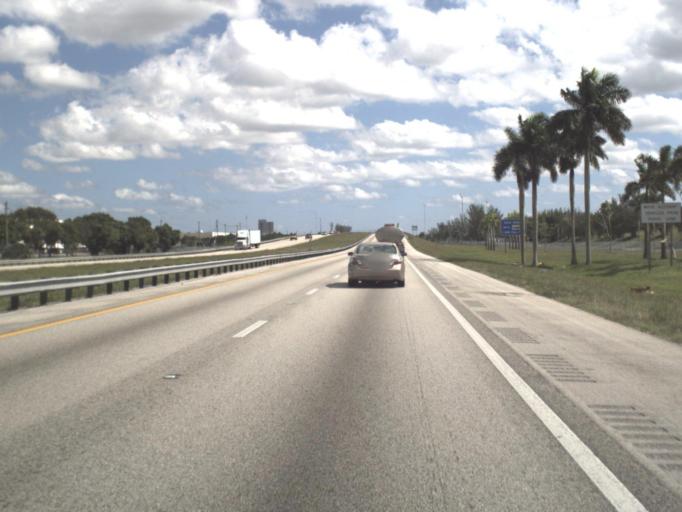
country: US
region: Florida
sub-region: Miami-Dade County
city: Country Club
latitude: 25.9711
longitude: -80.2840
